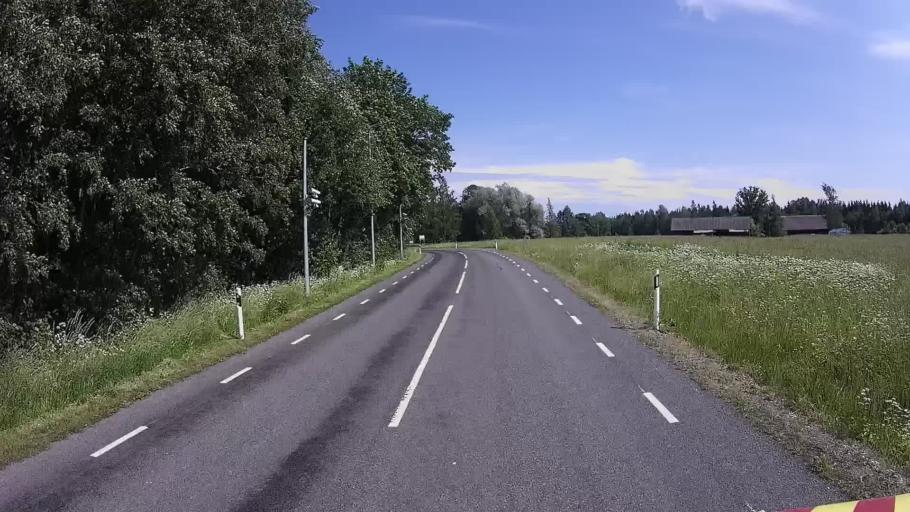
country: EE
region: Viljandimaa
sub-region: Karksi vald
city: Karksi-Nuia
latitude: 57.9936
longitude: 25.5323
